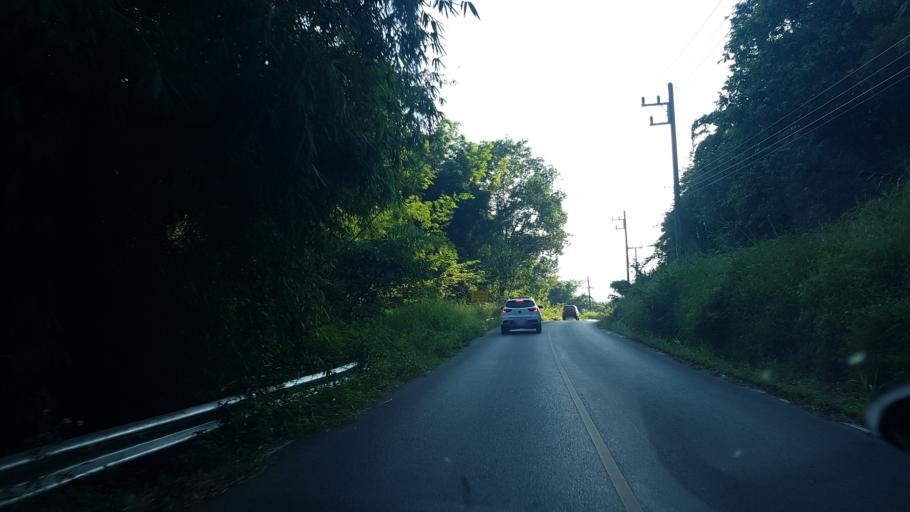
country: TH
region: Chiang Rai
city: Mae Fa Luang
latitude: 20.3183
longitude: 99.8184
